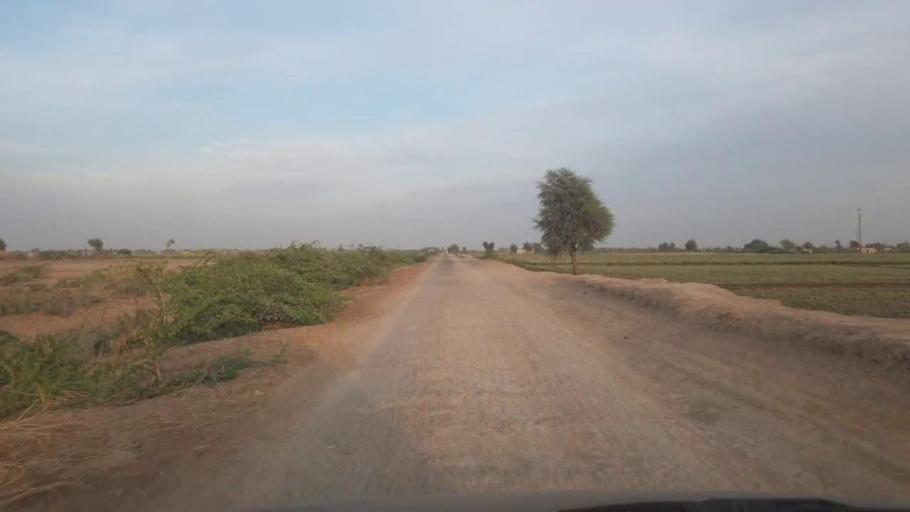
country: PK
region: Sindh
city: Kunri
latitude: 25.2122
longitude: 69.5789
